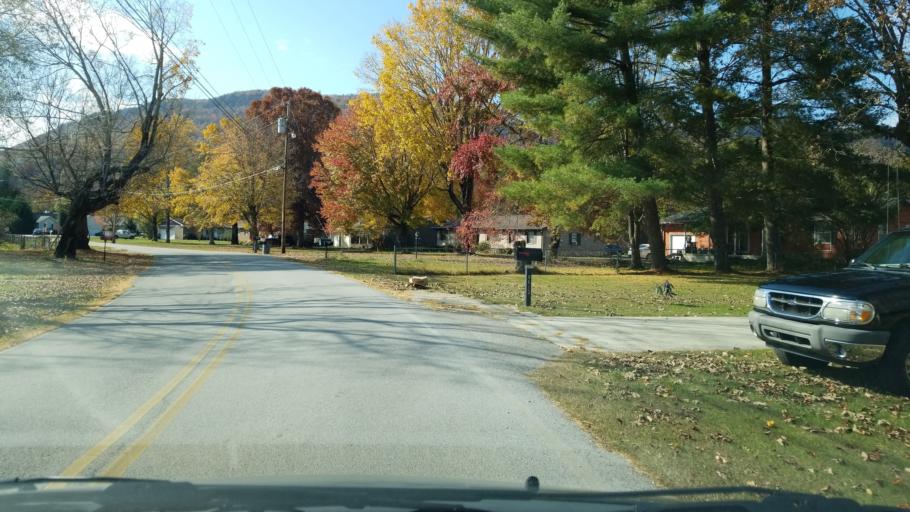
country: US
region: Tennessee
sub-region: Hamilton County
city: Soddy-Daisy
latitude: 35.2273
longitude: -85.2225
